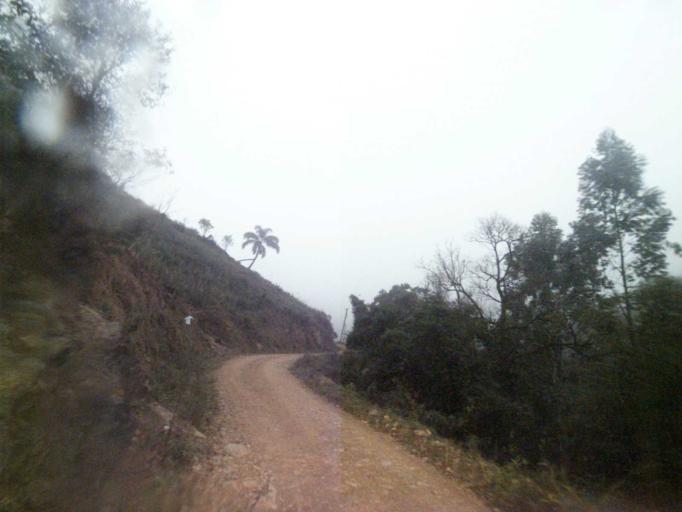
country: BR
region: Santa Catarina
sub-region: Anitapolis
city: Anitapolis
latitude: -27.8177
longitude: -49.1353
